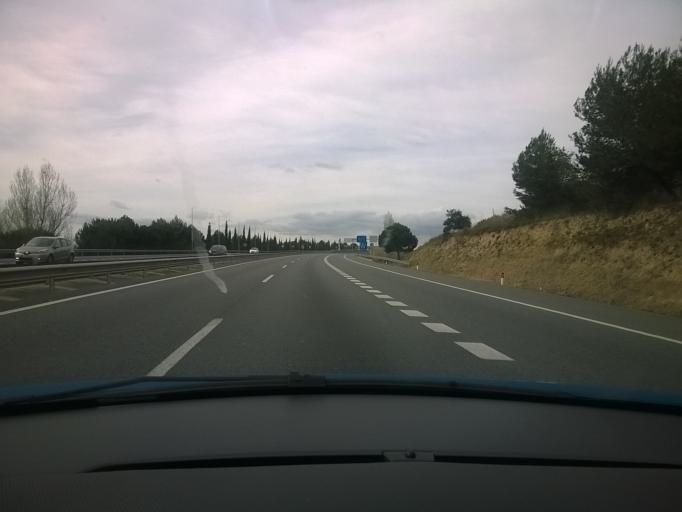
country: ES
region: Catalonia
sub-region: Provincia de Barcelona
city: Rubi
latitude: 41.4938
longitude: 2.0515
